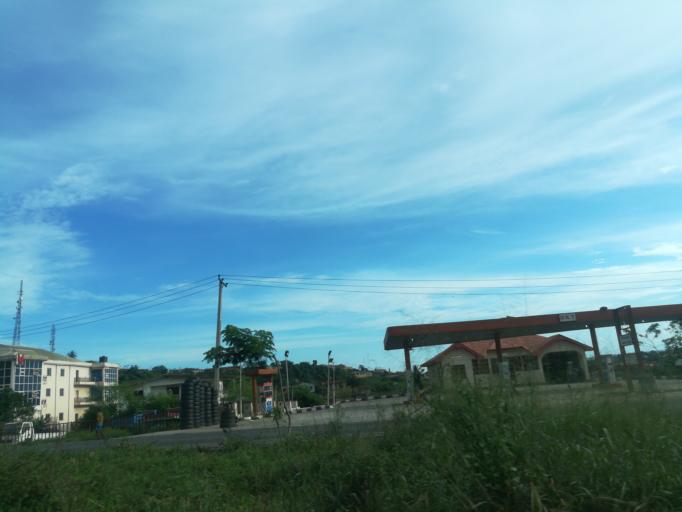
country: NG
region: Oyo
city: Ibadan
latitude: 7.3441
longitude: 3.9143
